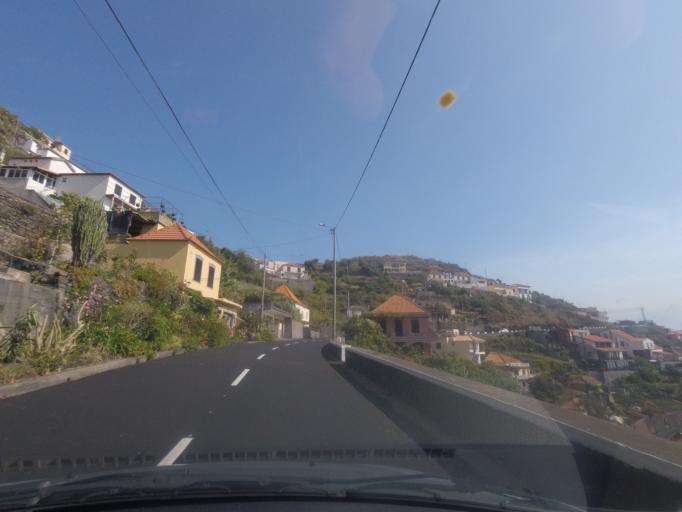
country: PT
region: Madeira
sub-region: Ribeira Brava
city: Campanario
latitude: 32.6692
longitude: -17.0379
